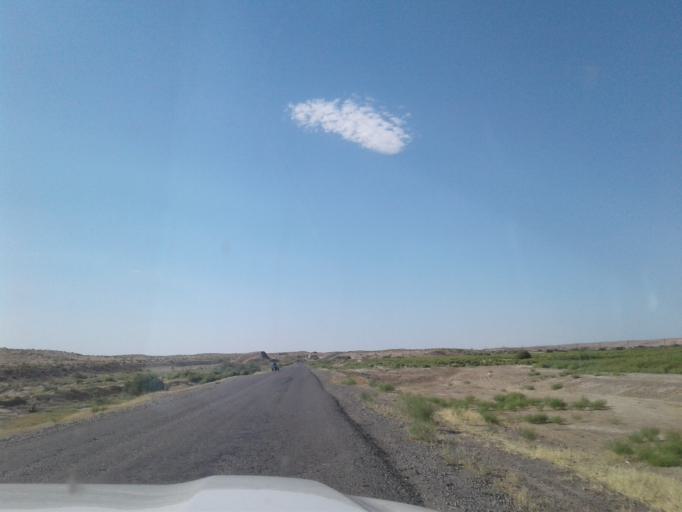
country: TM
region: Mary
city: Yoloeten
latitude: 36.6363
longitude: 62.4785
